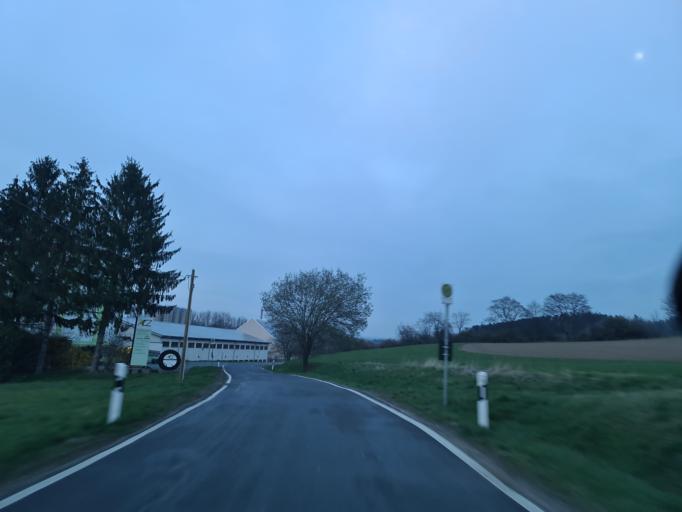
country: DE
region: Saxony
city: Oelsnitz
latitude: 50.4151
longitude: 12.1450
